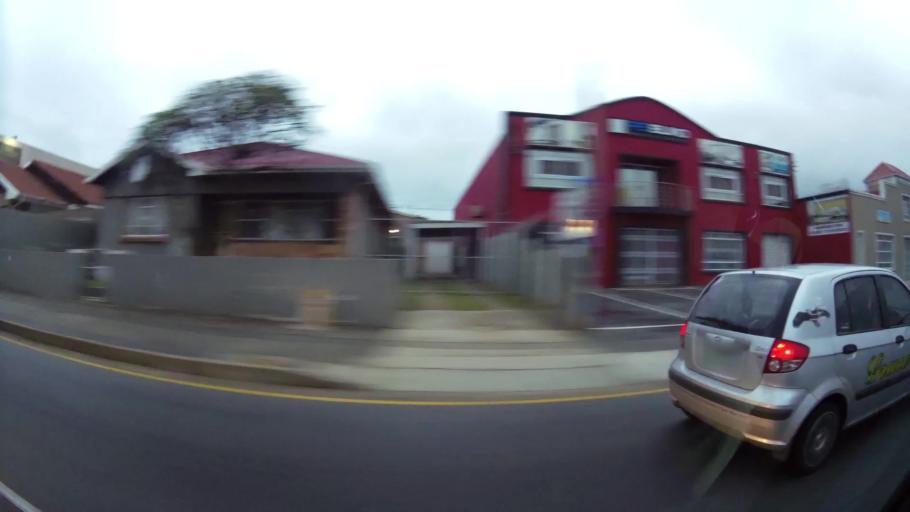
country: ZA
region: Eastern Cape
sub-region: Nelson Mandela Bay Metropolitan Municipality
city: Port Elizabeth
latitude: -33.9280
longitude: 25.5735
